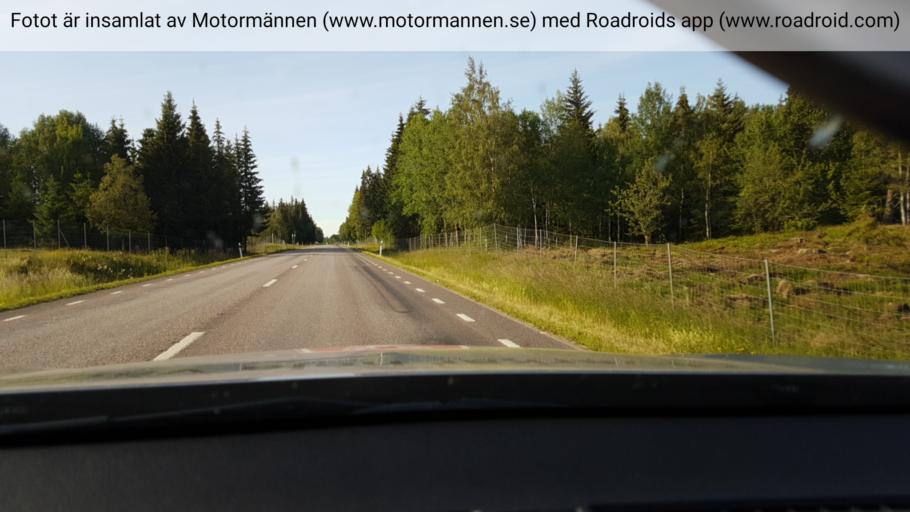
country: SE
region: Vaestra Goetaland
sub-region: Falkopings Kommun
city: Falkoeping
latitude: 58.0353
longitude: 13.5475
